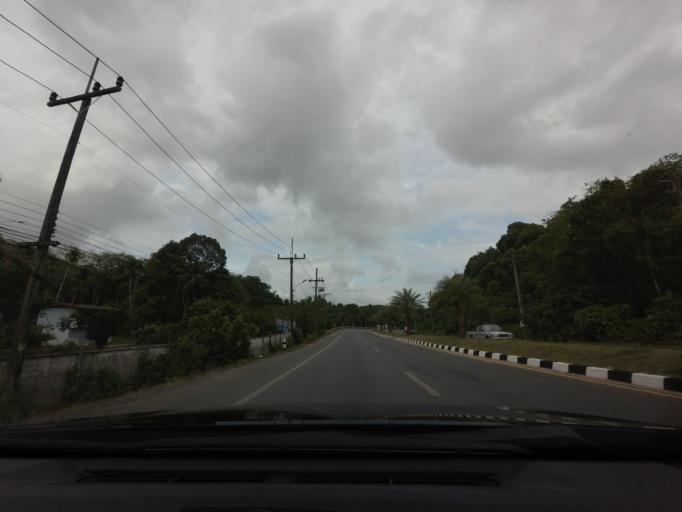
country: TH
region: Yala
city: Raman
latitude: 6.4728
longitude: 101.4147
